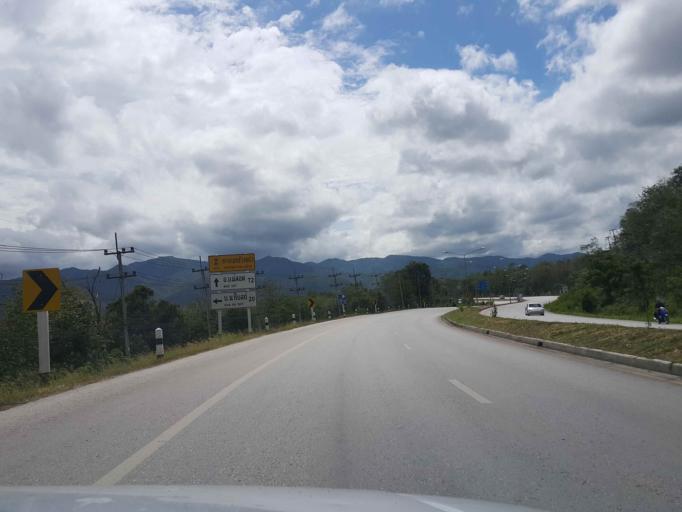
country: TH
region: Tak
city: Tak
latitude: 16.8047
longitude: 99.0504
